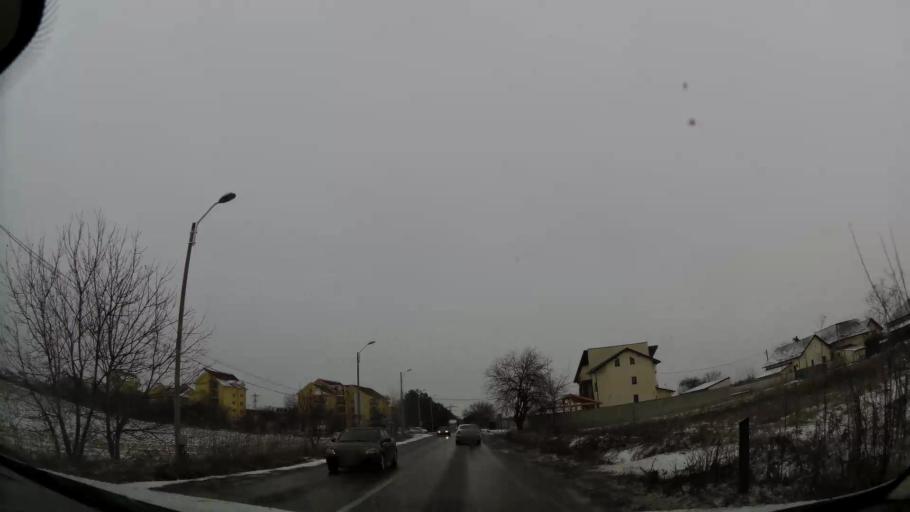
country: RO
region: Dambovita
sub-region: Comuna Ulmi
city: Ulmi
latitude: 44.9008
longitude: 25.5012
